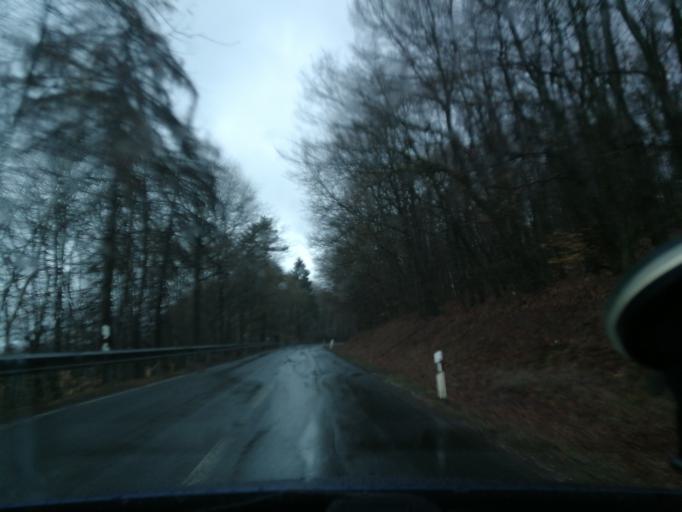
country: DE
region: Rheinland-Pfalz
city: Gielert
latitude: 49.7739
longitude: 7.0012
